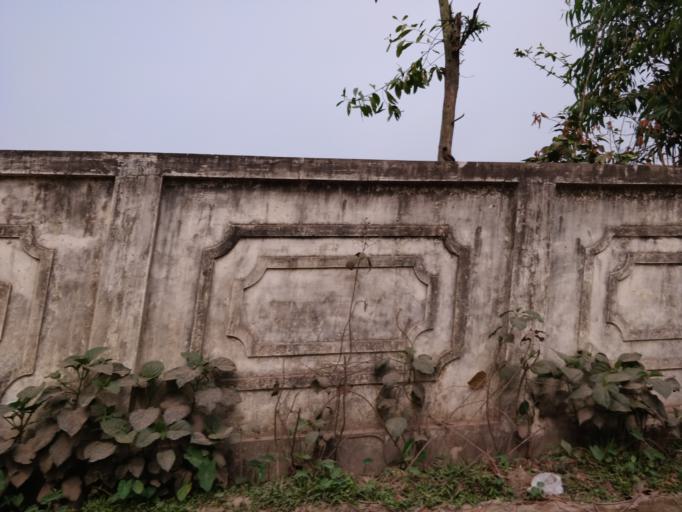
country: BD
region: Sylhet
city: Habiganj
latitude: 24.1694
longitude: 91.3549
